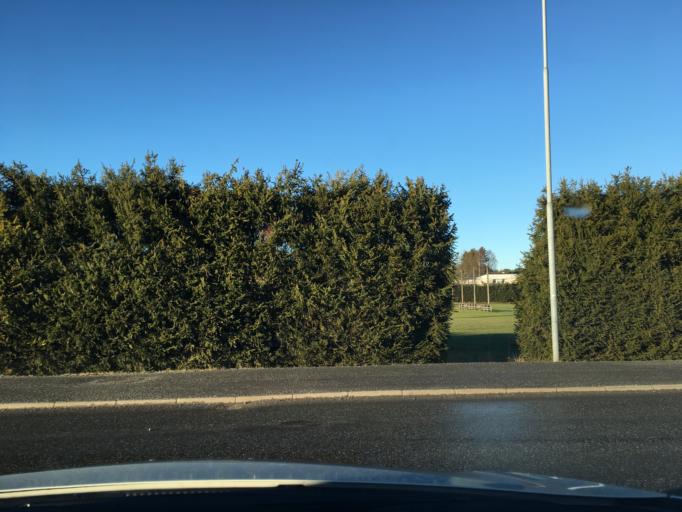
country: SE
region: Uppsala
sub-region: Knivsta Kommun
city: Knivsta
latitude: 59.7225
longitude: 17.7831
